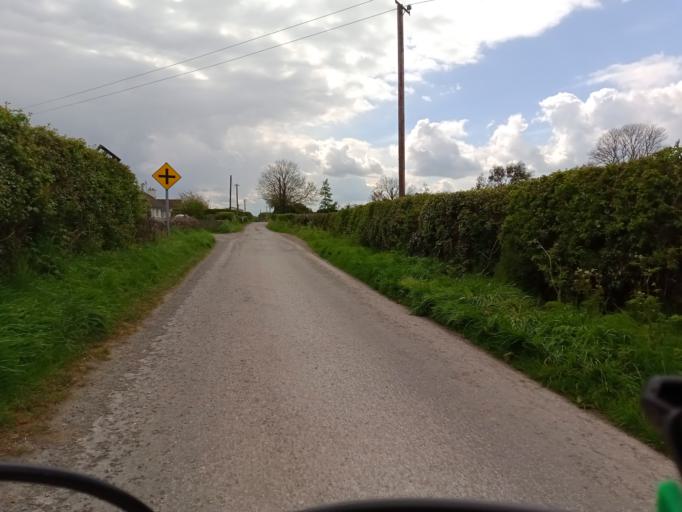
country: IE
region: Leinster
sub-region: Kilkenny
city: Kilkenny
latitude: 52.6246
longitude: -7.2919
